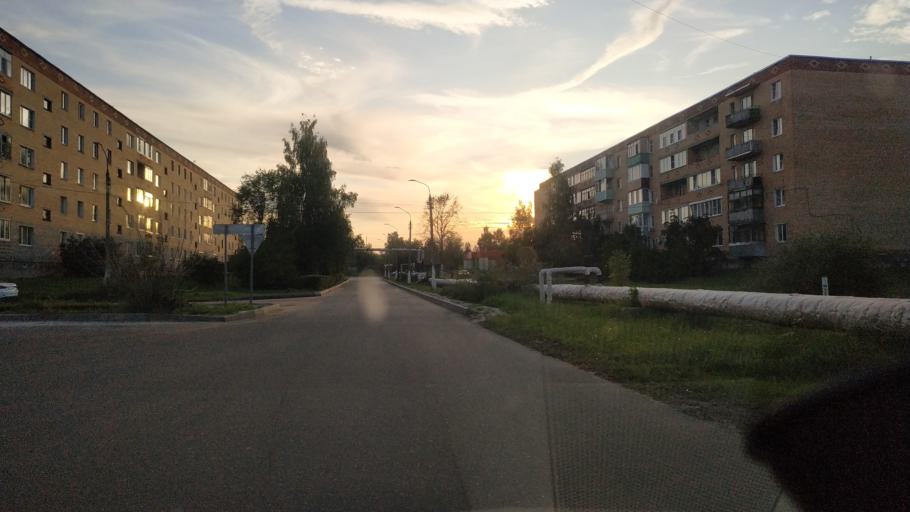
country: RU
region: Moskovskaya
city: Roshal'
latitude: 55.6666
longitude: 39.8523
